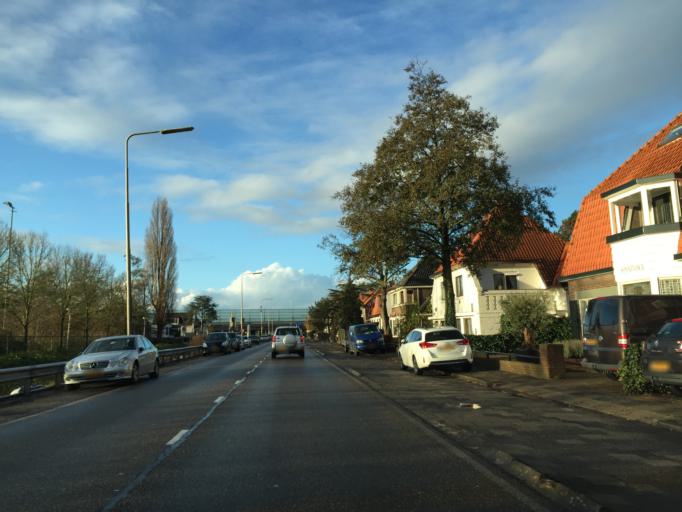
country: NL
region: South Holland
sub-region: Gemeente Delft
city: Delft
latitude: 52.0076
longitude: 4.3872
